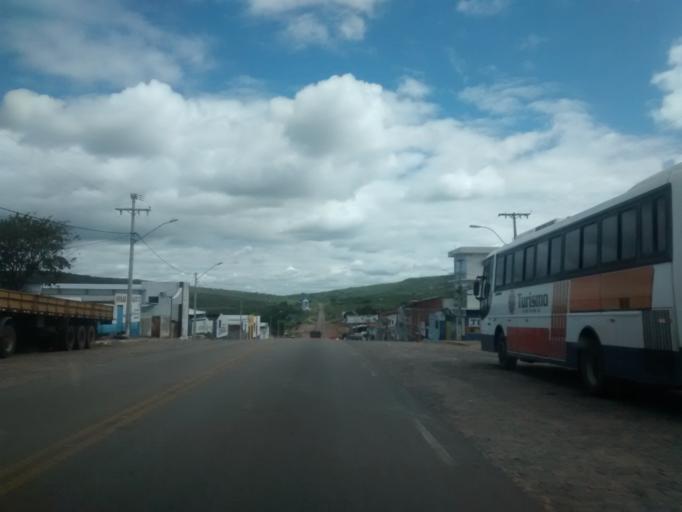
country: BR
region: Bahia
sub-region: Brumado
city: Brumado
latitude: -14.2171
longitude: -41.6835
